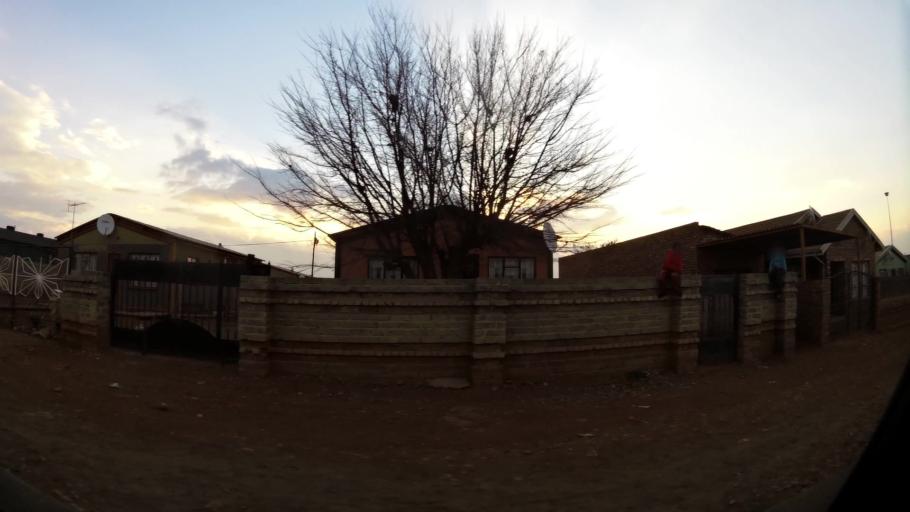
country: ZA
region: Gauteng
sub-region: City of Johannesburg Metropolitan Municipality
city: Orange Farm
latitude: -26.5550
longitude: 27.8628
